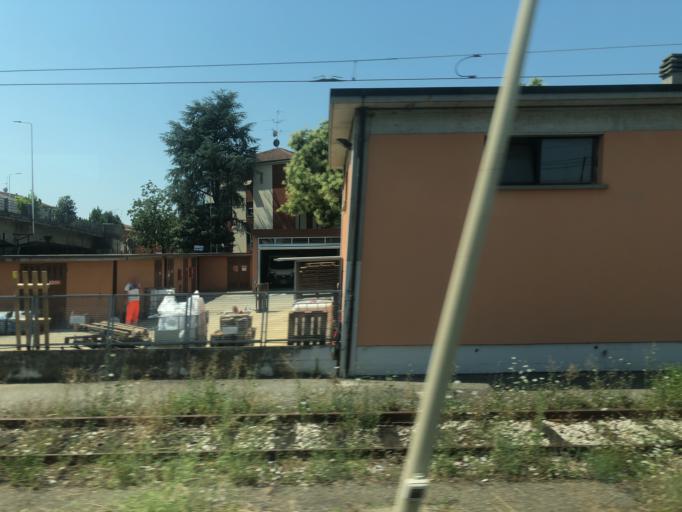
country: IT
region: Emilia-Romagna
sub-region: Provincia di Ravenna
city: Faenza
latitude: 44.2922
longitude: 11.8865
